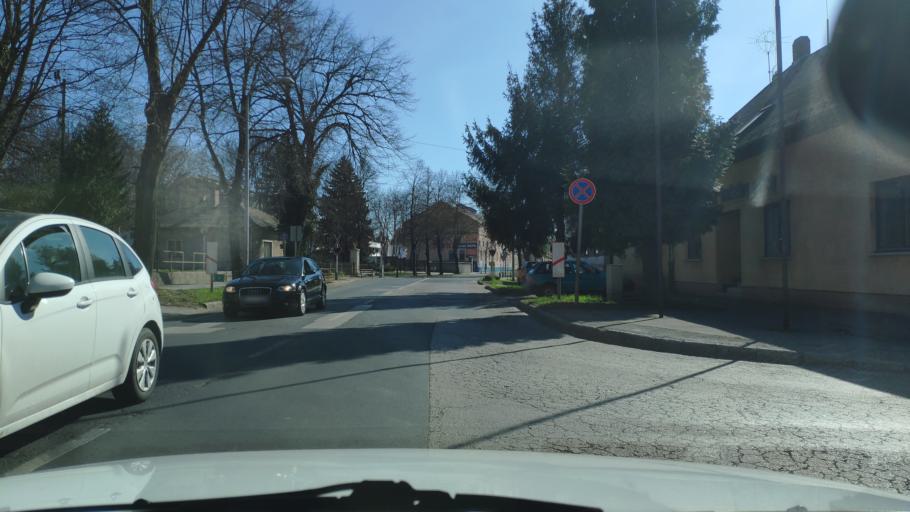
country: HU
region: Zala
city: Nagykanizsa
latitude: 46.4494
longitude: 16.9916
